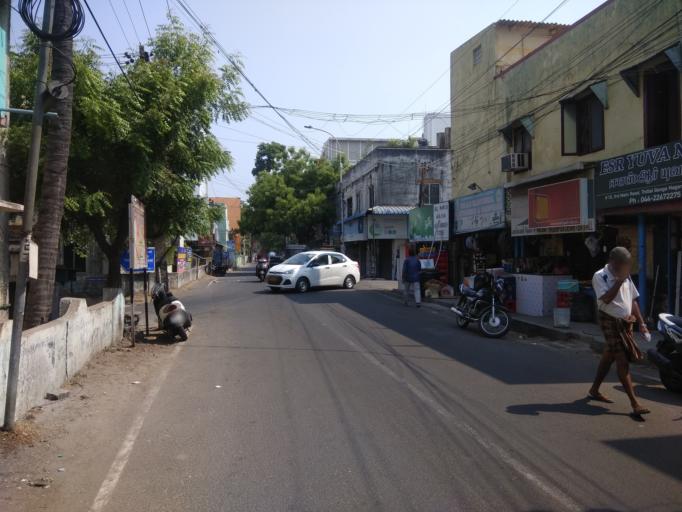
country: IN
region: Tamil Nadu
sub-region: Kancheepuram
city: Saint Thomas Mount
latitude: 12.9898
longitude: 80.1934
